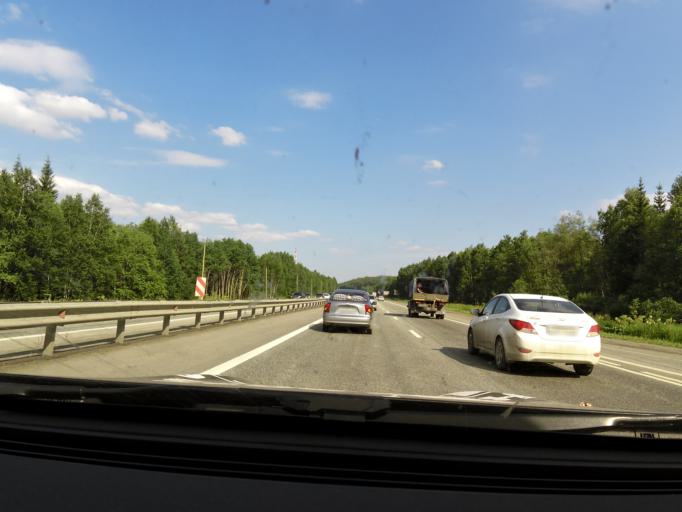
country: RU
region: Sverdlovsk
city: Severka
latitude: 56.8375
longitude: 60.2770
